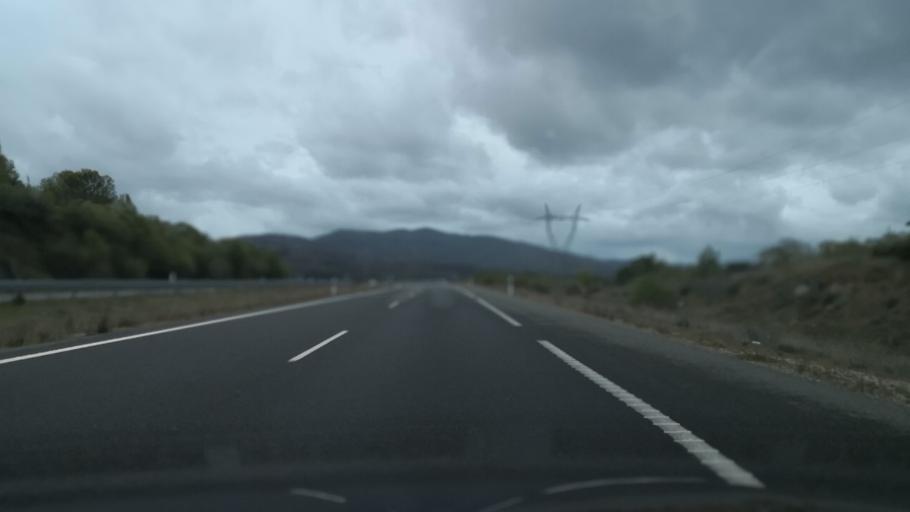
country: ES
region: Castille and Leon
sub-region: Provincia de Salamanca
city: Cantagallo
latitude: 40.3658
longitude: -5.8332
